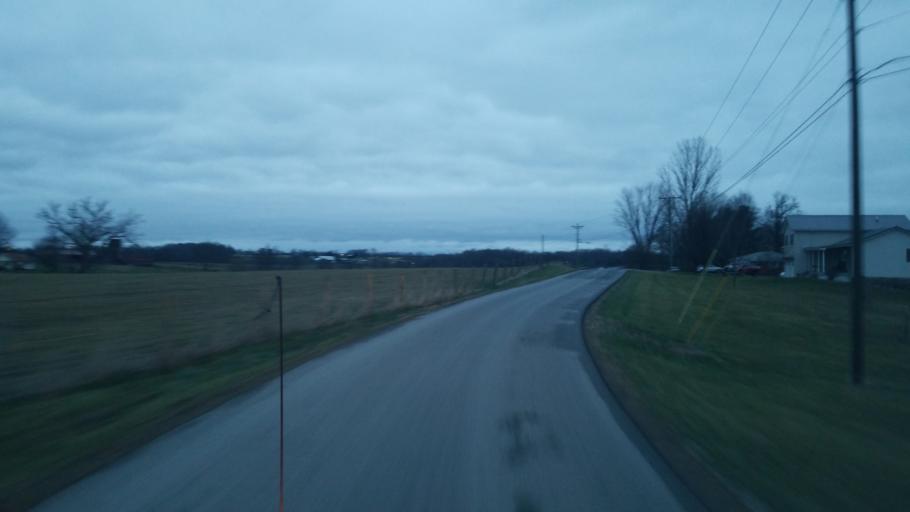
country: US
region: Kentucky
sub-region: Fleming County
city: Flemingsburg
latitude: 38.4911
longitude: -83.6607
